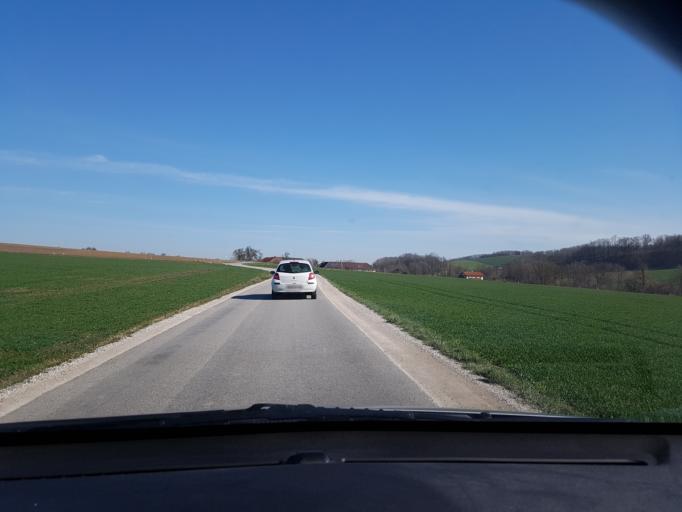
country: AT
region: Upper Austria
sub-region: Politischer Bezirk Linz-Land
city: Ansfelden
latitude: 48.2001
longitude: 14.3124
